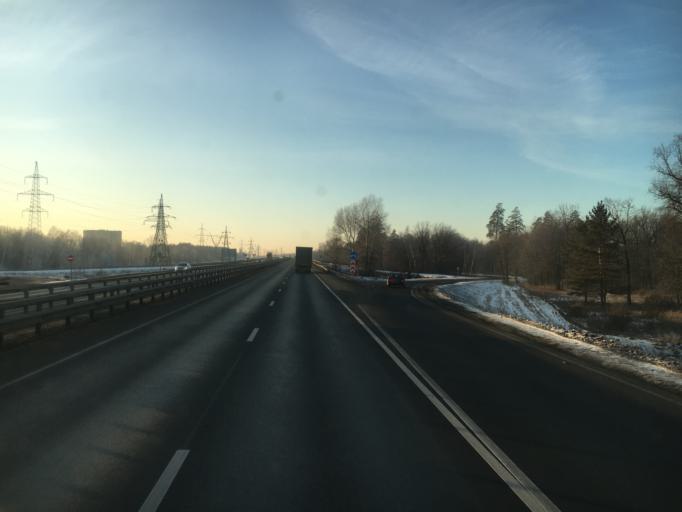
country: RU
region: Samara
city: Pribrezhnyy
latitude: 53.5172
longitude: 49.8428
